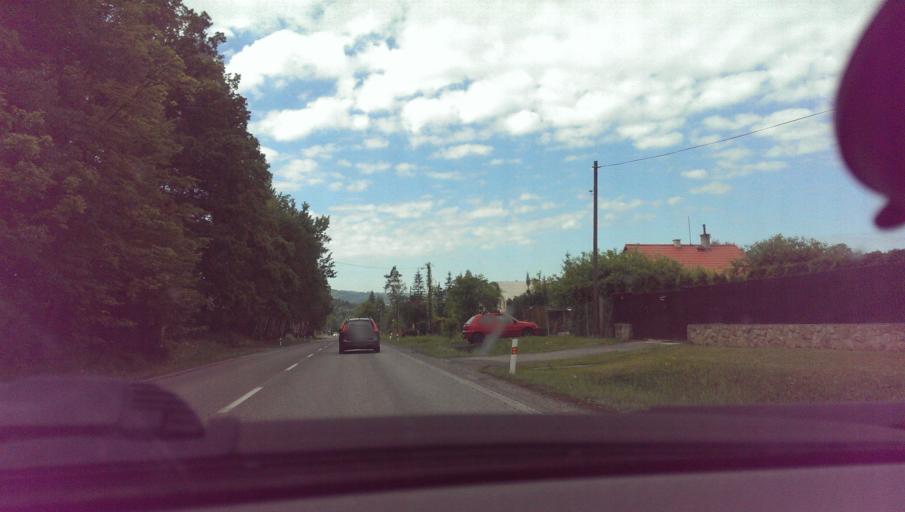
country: CZ
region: Zlin
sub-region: Okres Vsetin
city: Roznov pod Radhostem
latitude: 49.4758
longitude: 18.1641
